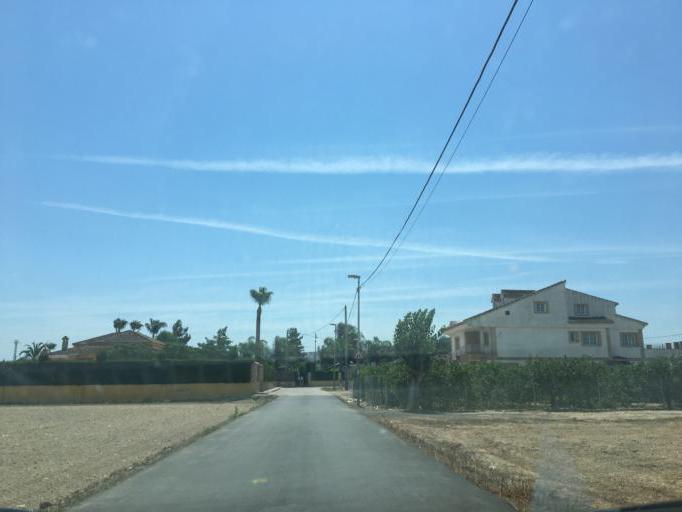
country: ES
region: Murcia
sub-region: Murcia
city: Santomera
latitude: 38.0226
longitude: -1.0579
